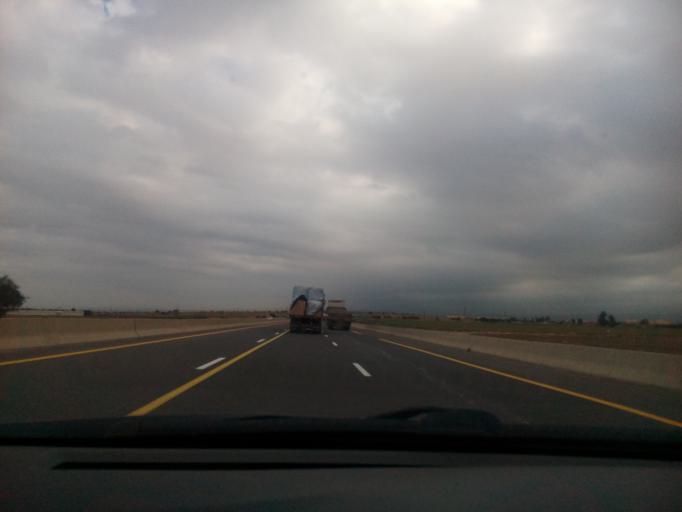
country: DZ
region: Relizane
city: Relizane
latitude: 35.7984
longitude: 0.5135
